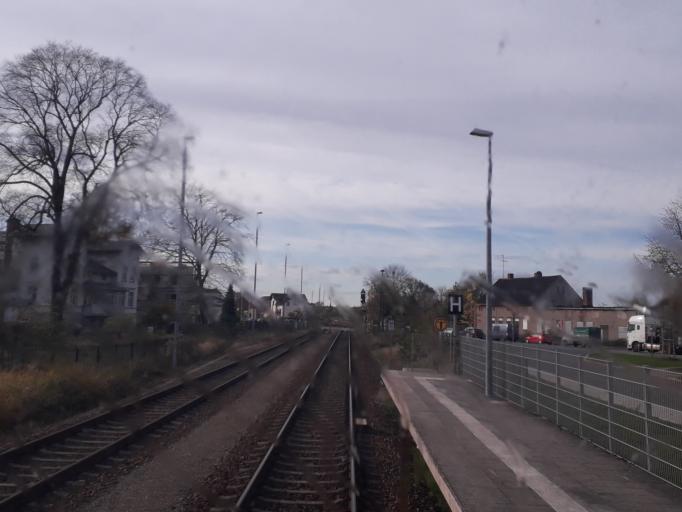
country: DE
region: Brandenburg
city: Wittstock
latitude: 53.1608
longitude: 12.4768
